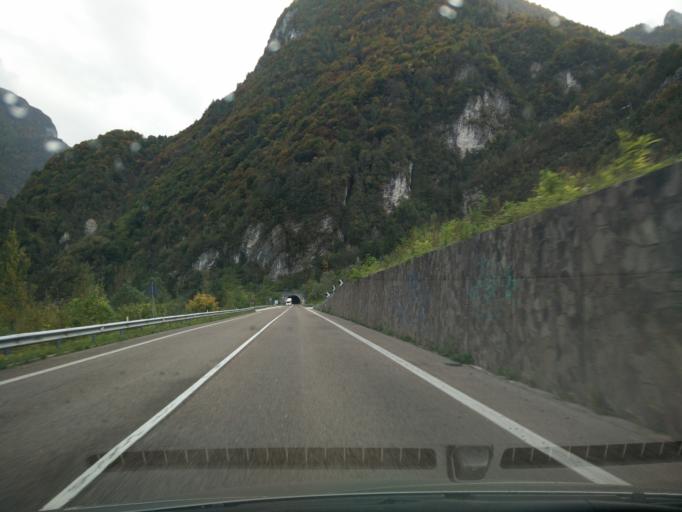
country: IT
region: Veneto
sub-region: Provincia di Belluno
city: Ospitale di Cadore
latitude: 46.3212
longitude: 12.3175
